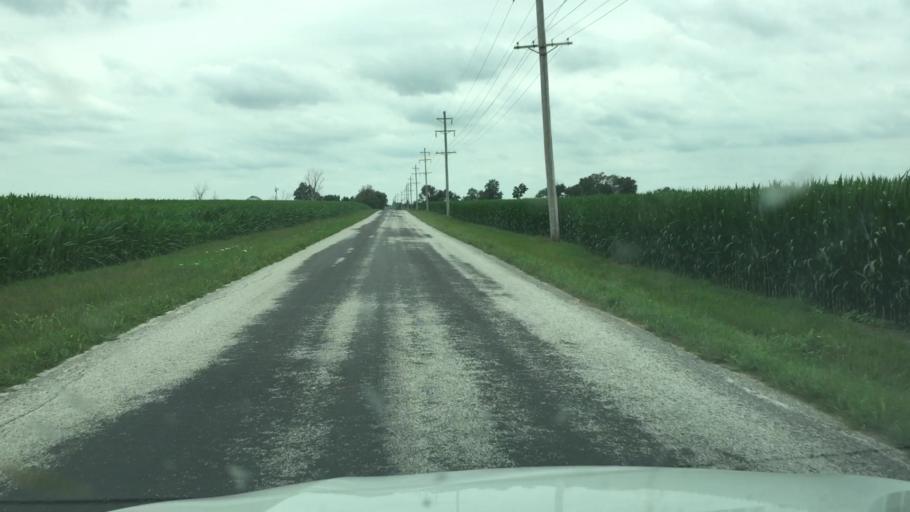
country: US
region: Illinois
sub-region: Hancock County
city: Carthage
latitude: 40.3928
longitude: -91.0826
